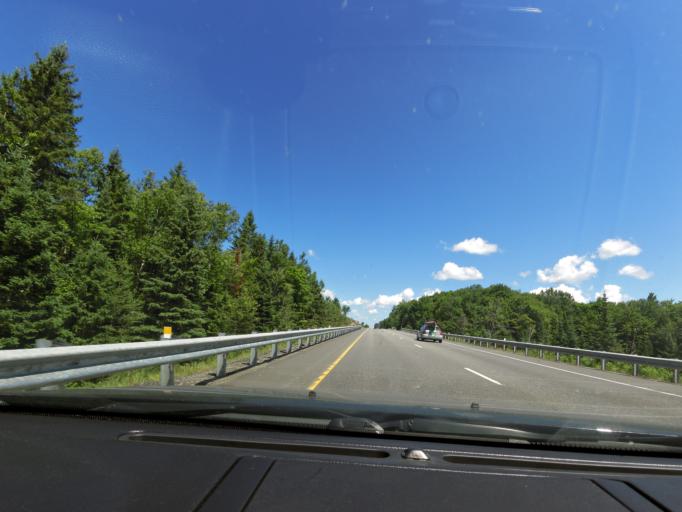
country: CA
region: Ontario
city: Bracebridge
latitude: 45.1451
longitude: -79.3111
